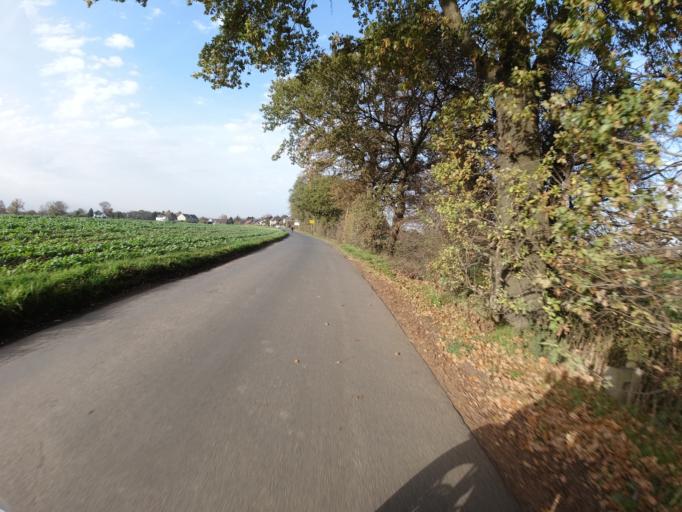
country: DE
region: North Rhine-Westphalia
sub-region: Regierungsbezirk Dusseldorf
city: Moers
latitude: 51.4158
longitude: 6.6223
